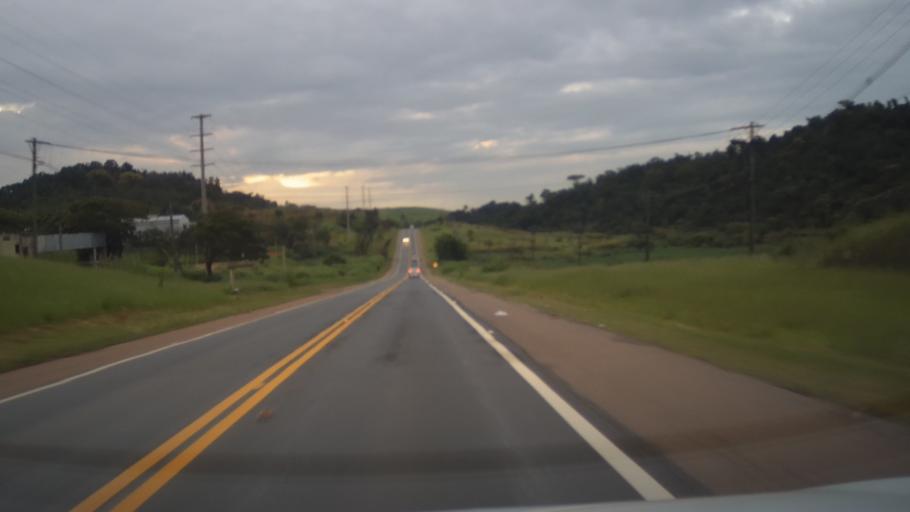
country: BR
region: Sao Paulo
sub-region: Vinhedo
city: Vinhedo
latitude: -23.0622
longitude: -47.0137
